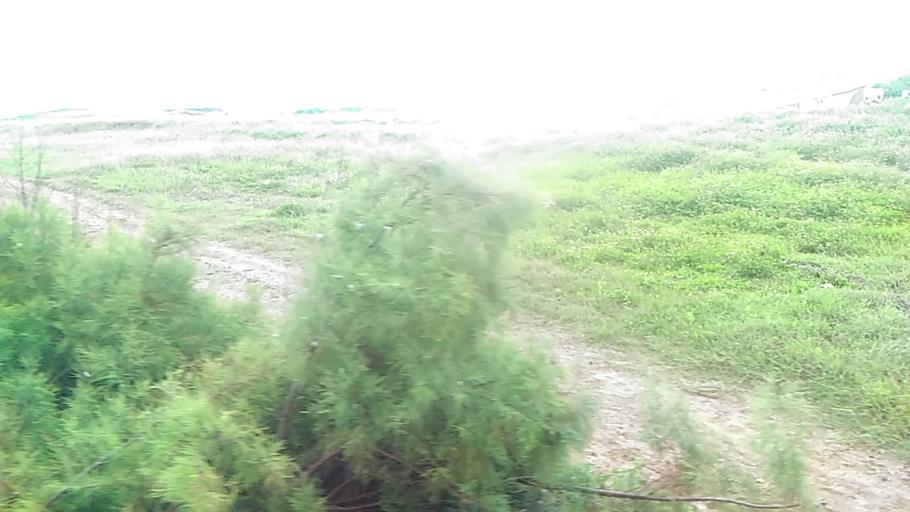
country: TW
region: Taiwan
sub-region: Penghu
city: Ma-kung
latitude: 23.3790
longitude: 119.5026
